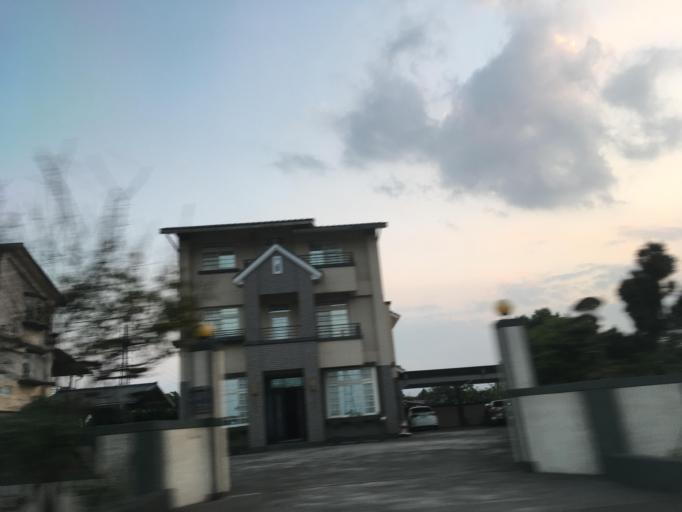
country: TW
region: Taiwan
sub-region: Yilan
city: Yilan
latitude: 24.6891
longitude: 121.7893
